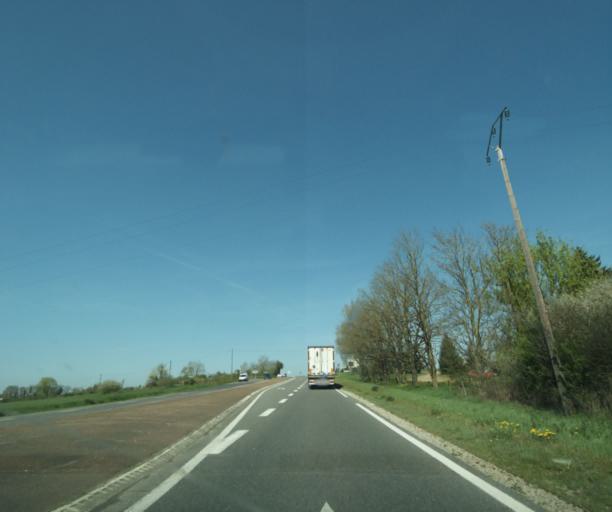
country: FR
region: Bourgogne
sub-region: Departement de la Nievre
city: Chantenay-Saint-Imbert
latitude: 46.7350
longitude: 3.1661
